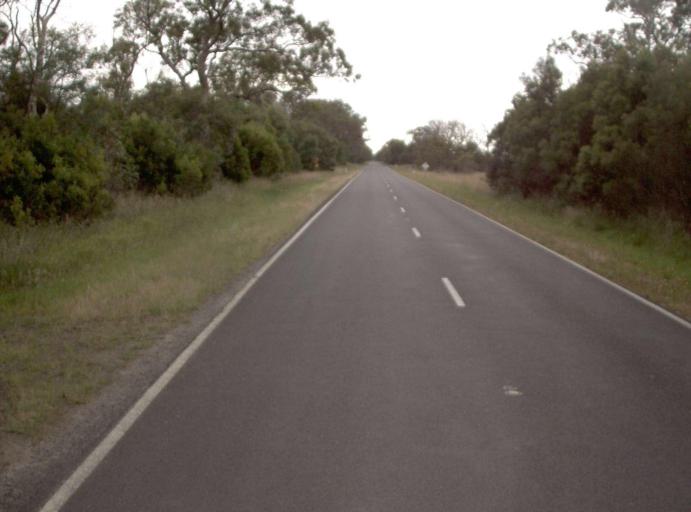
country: AU
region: Victoria
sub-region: Latrobe
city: Traralgon
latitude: -38.5579
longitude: 146.8092
